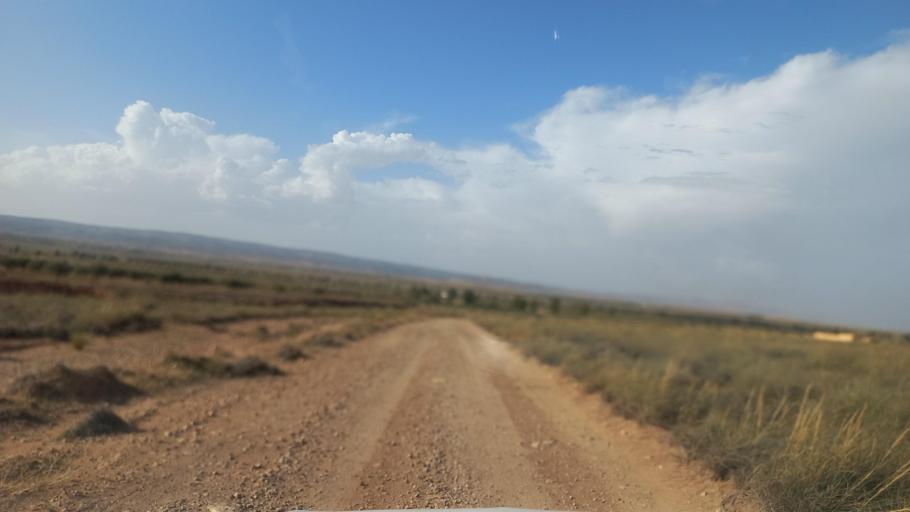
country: TN
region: Al Qasrayn
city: Kasserine
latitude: 35.2204
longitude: 8.9697
